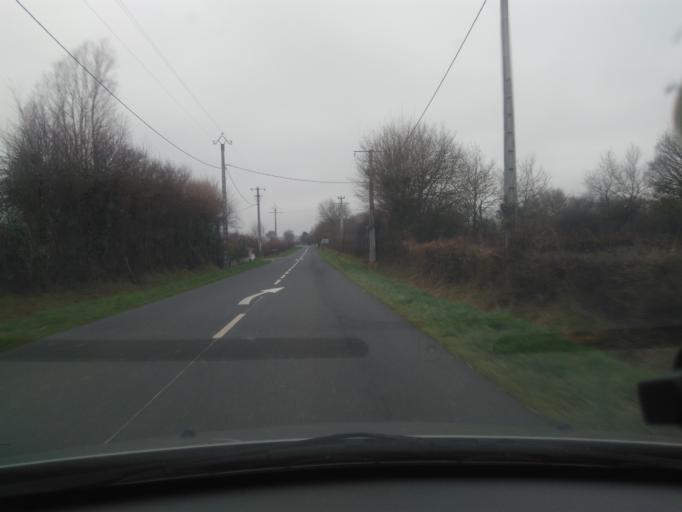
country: FR
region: Centre
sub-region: Departement de l'Indre
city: Montgivray
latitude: 46.6389
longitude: 2.0806
